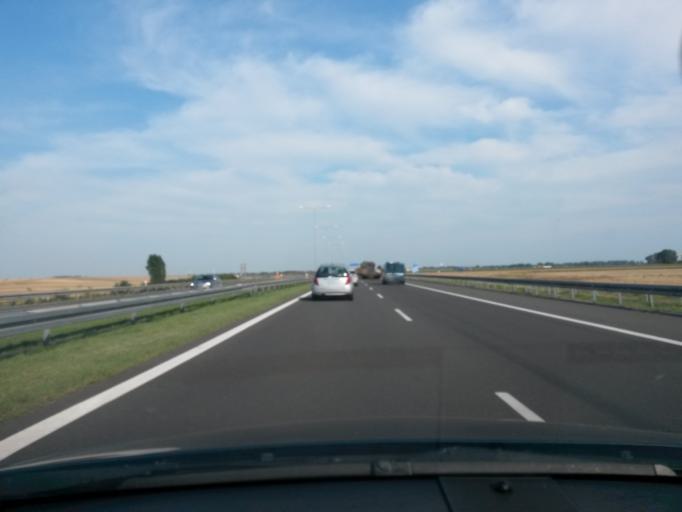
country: PL
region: Greater Poland Voivodeship
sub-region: Powiat slupecki
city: Strzalkowo
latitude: 52.2567
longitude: 17.8060
